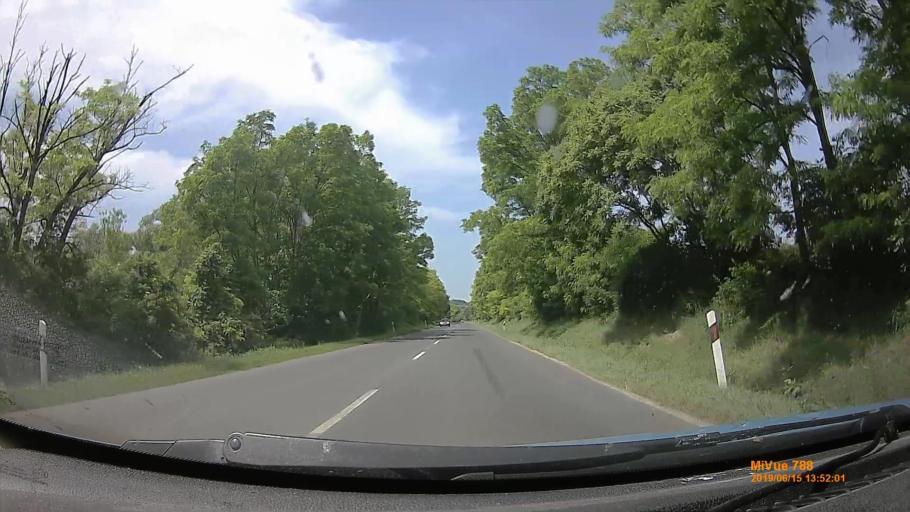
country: HU
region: Tolna
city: Iregszemcse
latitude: 46.7609
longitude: 18.1572
